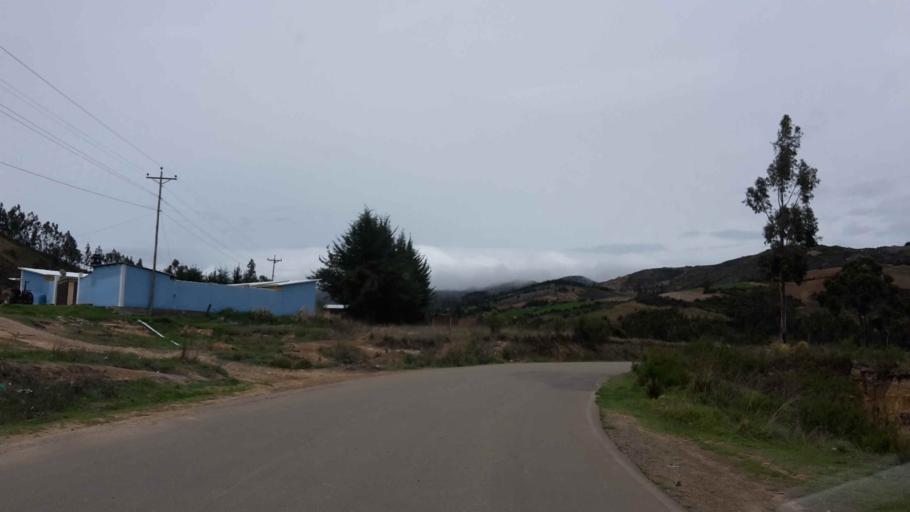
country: BO
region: Cochabamba
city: Totora
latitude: -17.6876
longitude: -65.2154
